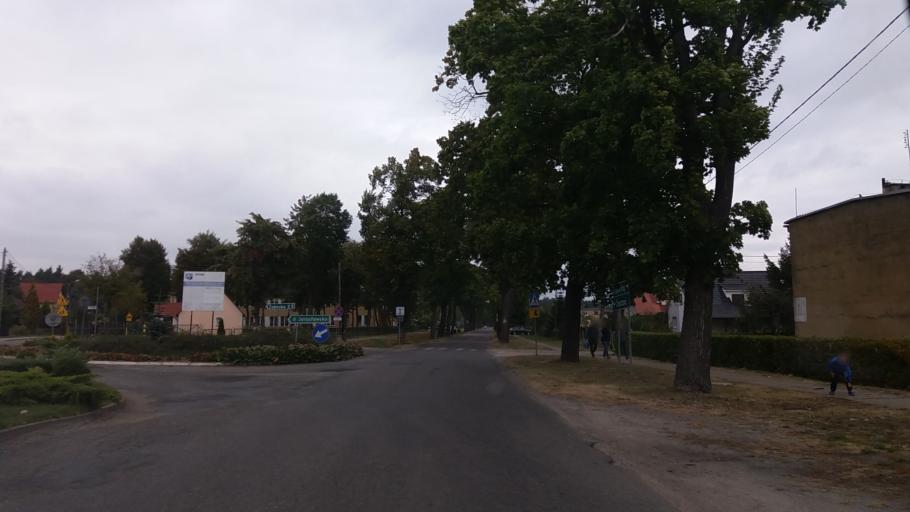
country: PL
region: Lubusz
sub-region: Powiat strzelecko-drezdenecki
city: Strzelce Krajenskie
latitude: 52.9541
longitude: 15.4524
